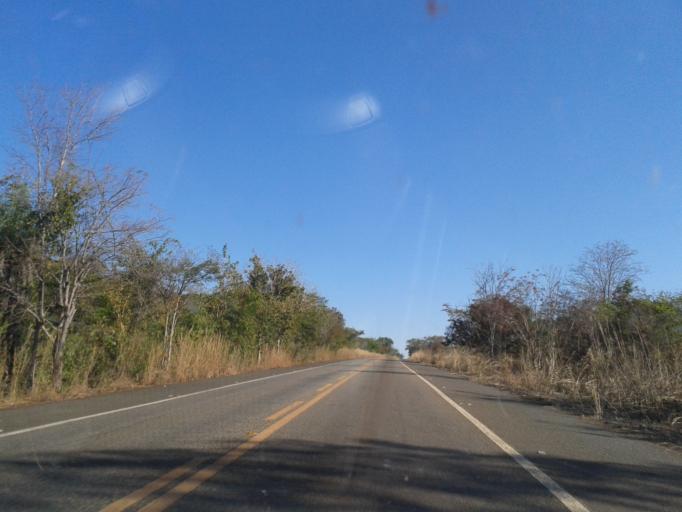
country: BR
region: Goias
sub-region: Mozarlandia
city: Mozarlandia
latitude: -15.0404
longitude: -50.6050
